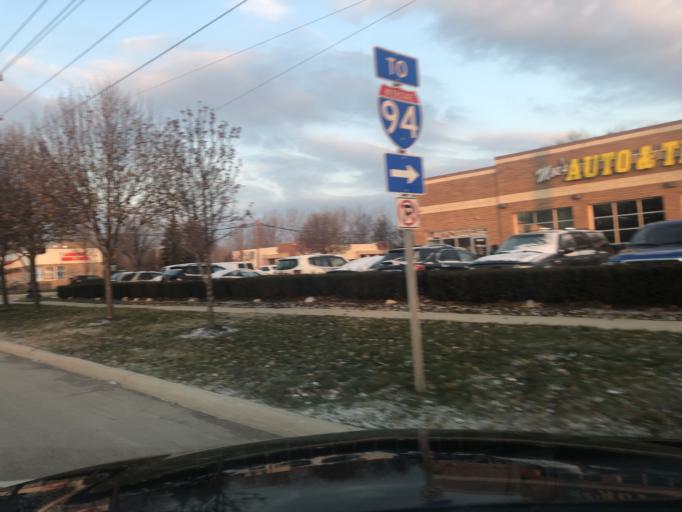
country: US
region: Michigan
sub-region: Wayne County
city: Romulus
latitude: 42.2232
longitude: -83.3847
